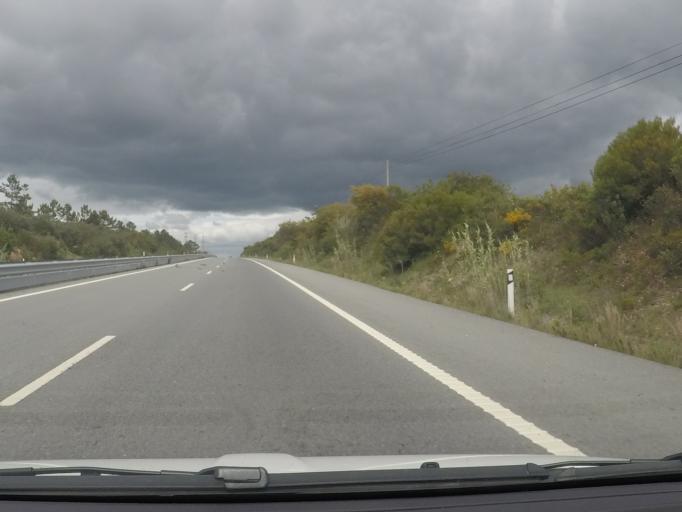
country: PT
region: Setubal
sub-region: Santiago do Cacem
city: Santo Andre
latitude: 37.9902
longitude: -8.7704
